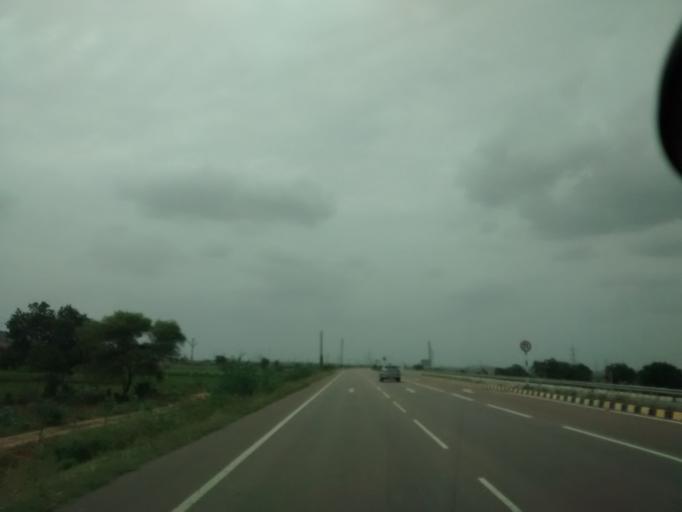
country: IN
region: Andhra Pradesh
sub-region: Kurnool
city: Ramapuram
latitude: 15.1180
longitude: 77.6606
